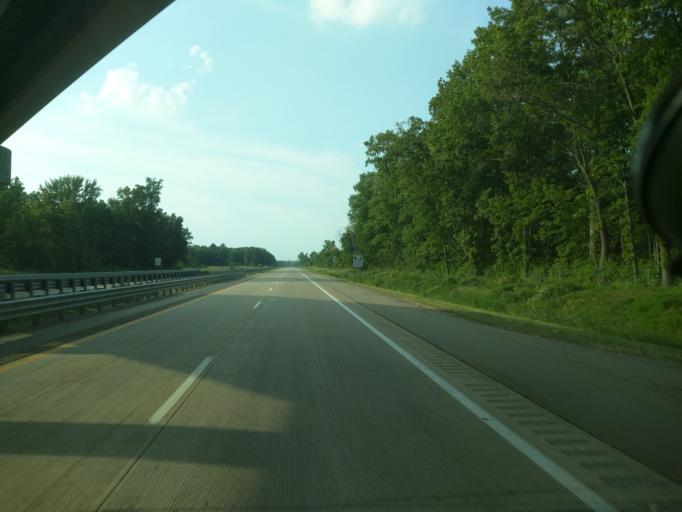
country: US
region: Michigan
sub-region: Jackson County
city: Jackson
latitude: 42.2966
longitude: -84.4327
